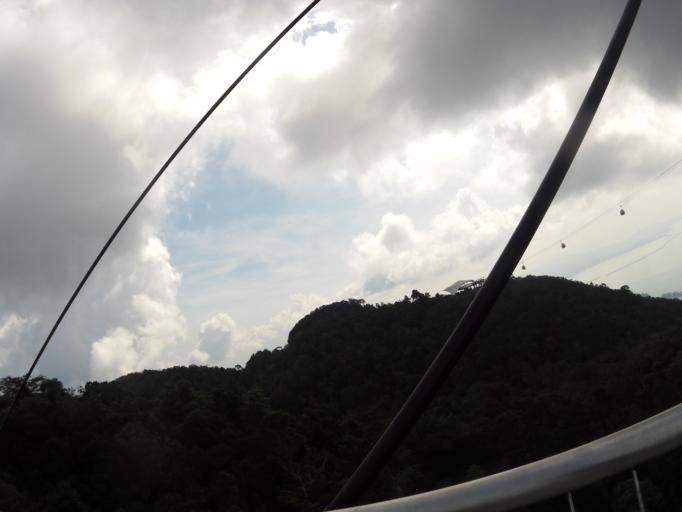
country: MY
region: Kedah
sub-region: Langkawi
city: Kuah
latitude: 6.3869
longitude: 99.6620
